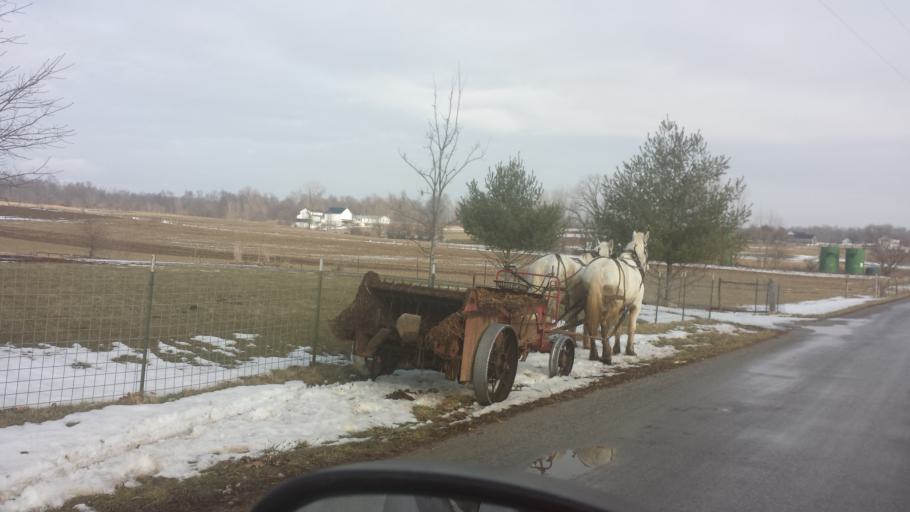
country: US
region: Ohio
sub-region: Morrow County
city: Mount Gilead
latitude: 40.5649
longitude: -82.6931
